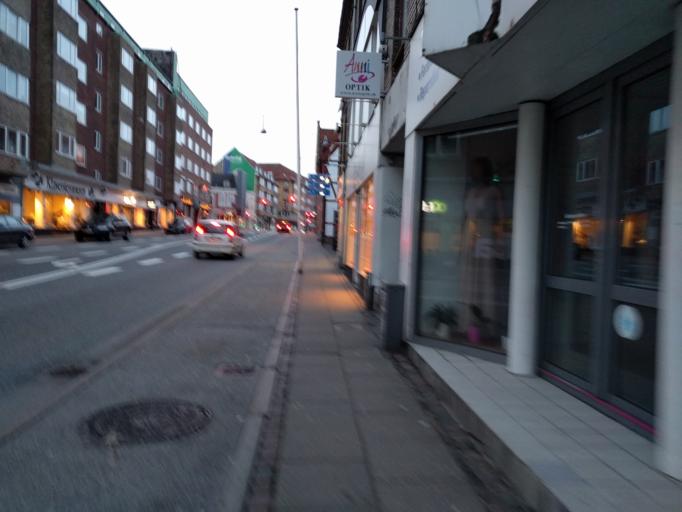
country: DK
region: North Denmark
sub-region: Alborg Kommune
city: Aalborg
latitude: 57.0492
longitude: 9.9162
